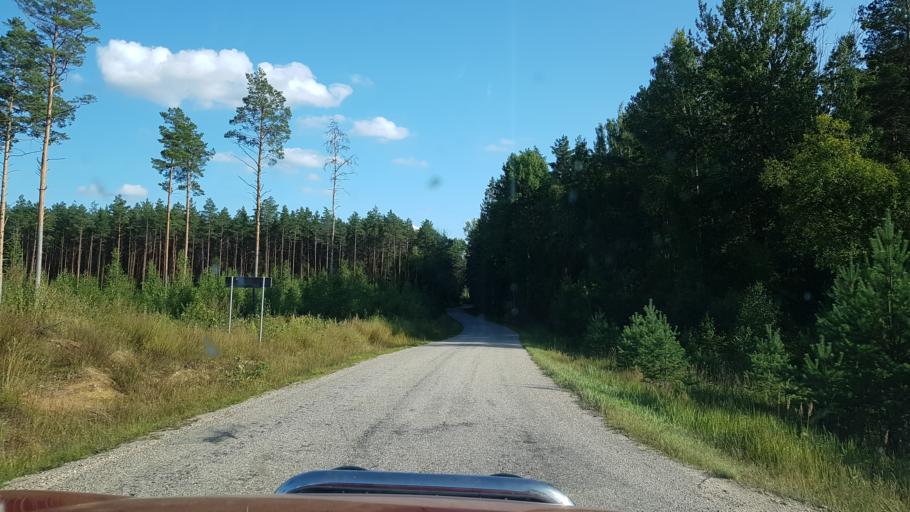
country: EE
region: Vorumaa
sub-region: Voru linn
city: Voru
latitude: 57.8872
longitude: 27.1061
